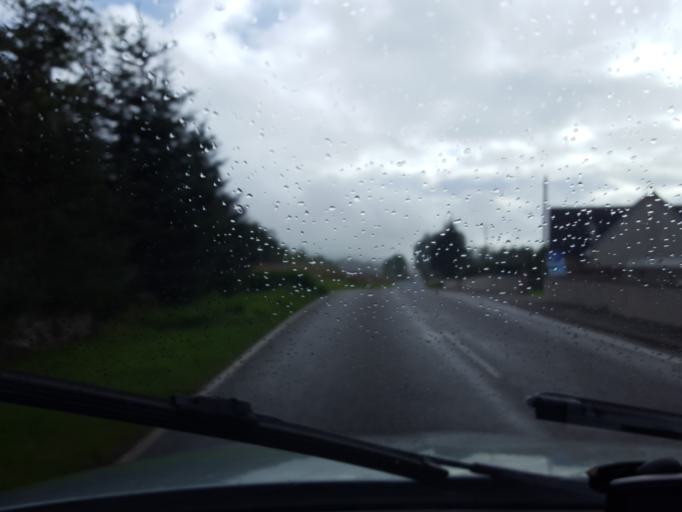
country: GB
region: Scotland
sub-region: Aberdeenshire
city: Laurencekirk
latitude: 56.8756
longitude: -2.4077
